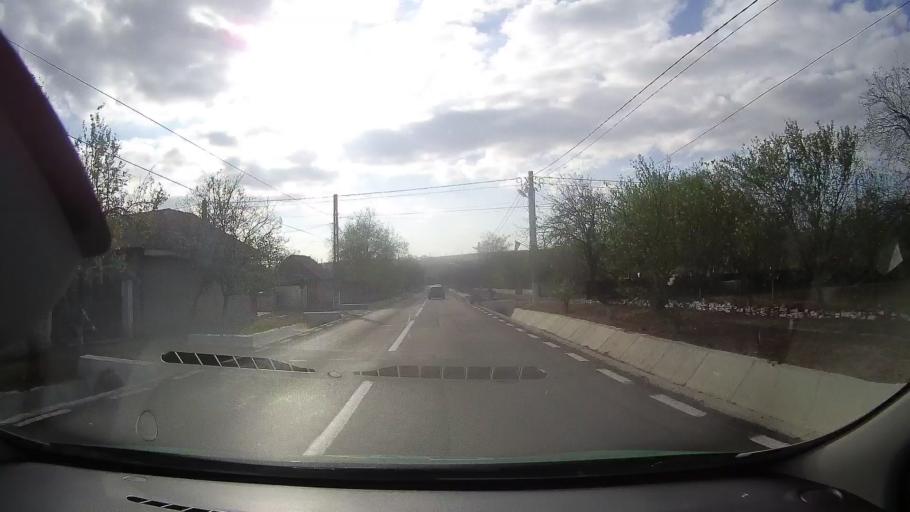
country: RO
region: Tulcea
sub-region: Comuna Topolog
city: Topolog
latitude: 44.8845
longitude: 28.3820
